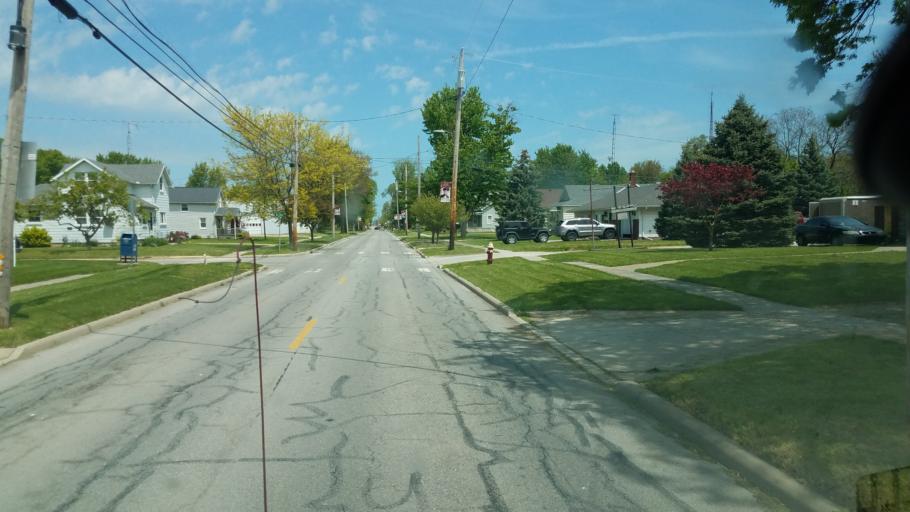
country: US
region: Ohio
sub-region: Ottawa County
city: Oak Harbor
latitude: 41.5128
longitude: -83.1450
